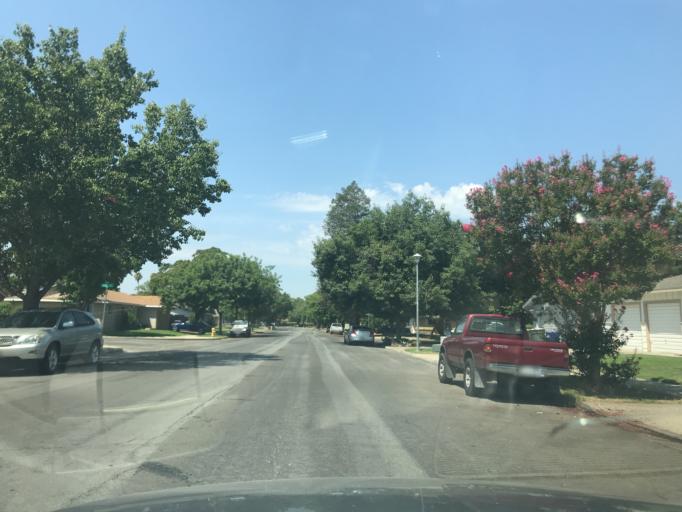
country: US
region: California
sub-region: Merced County
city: Merced
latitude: 37.3298
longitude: -120.4797
